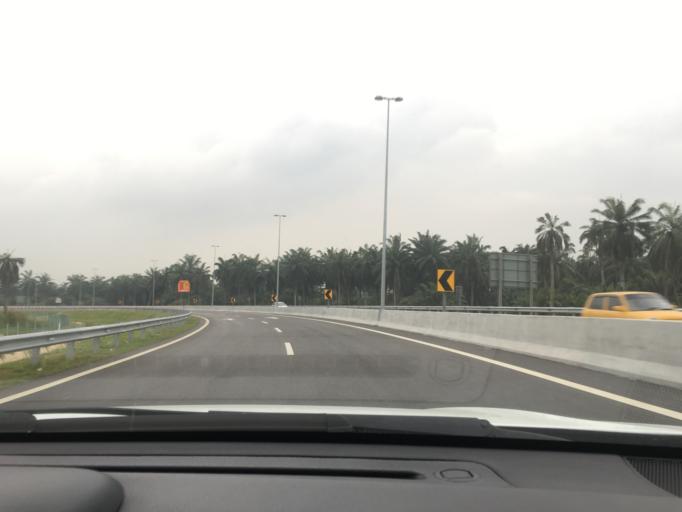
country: MY
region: Selangor
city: Klang
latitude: 3.1285
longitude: 101.3995
